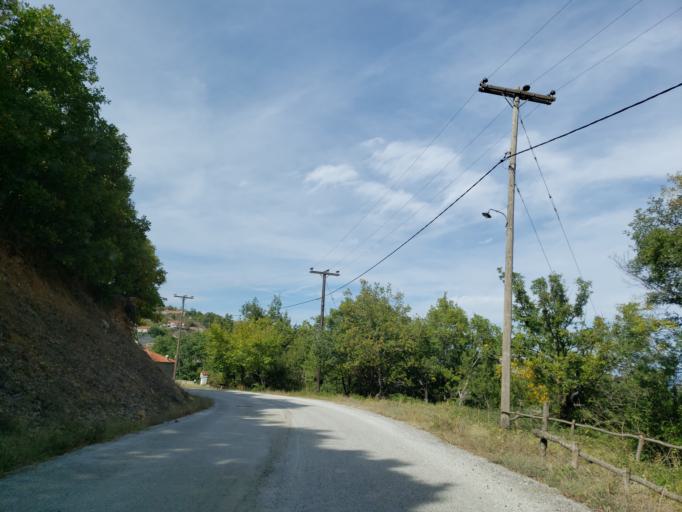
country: GR
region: Thessaly
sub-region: Trikala
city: Kastraki
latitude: 39.7737
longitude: 21.6612
